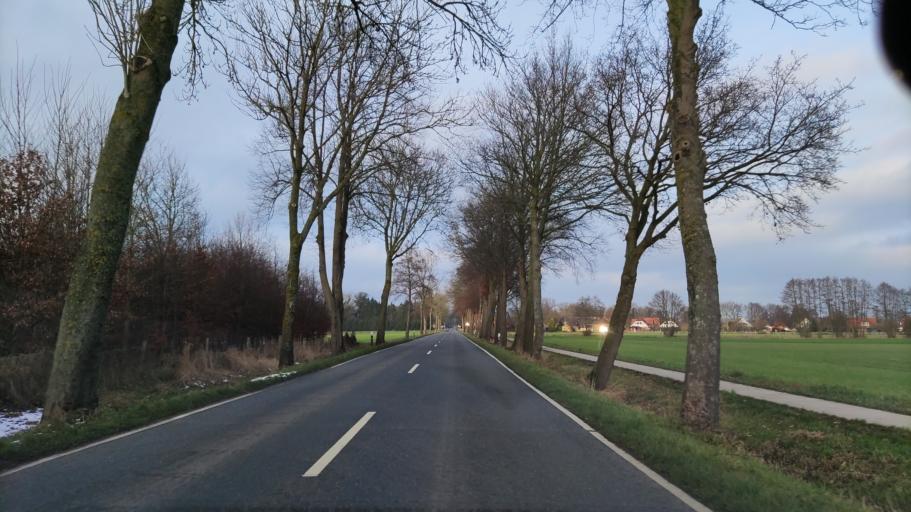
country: DE
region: Lower Saxony
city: Ludersburg
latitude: 53.3133
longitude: 10.5727
